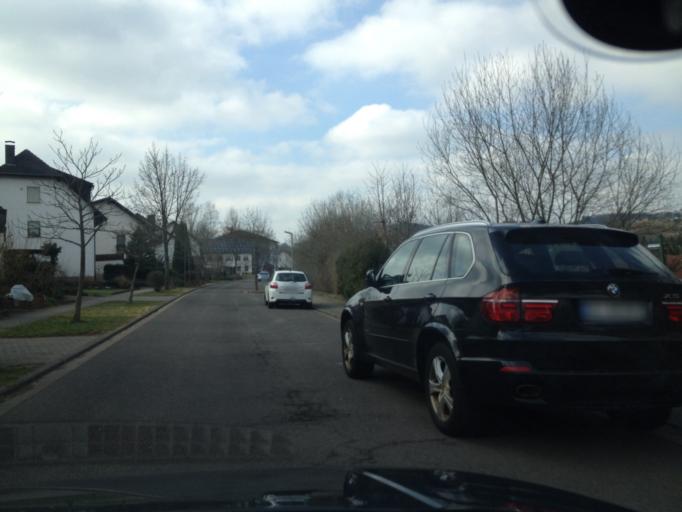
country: DE
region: Saarland
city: Ottweiler
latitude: 49.4061
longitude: 7.1527
